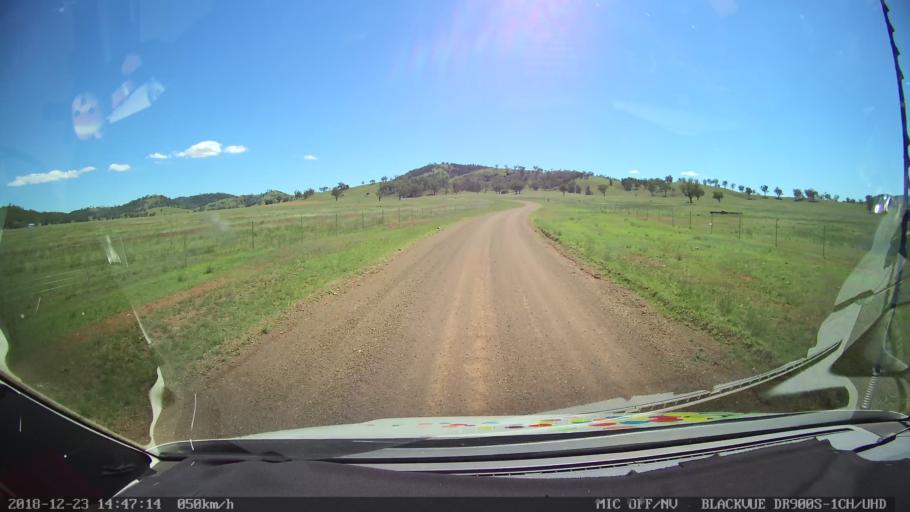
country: AU
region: New South Wales
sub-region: Tamworth Municipality
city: Manilla
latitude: -30.6531
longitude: 150.8745
